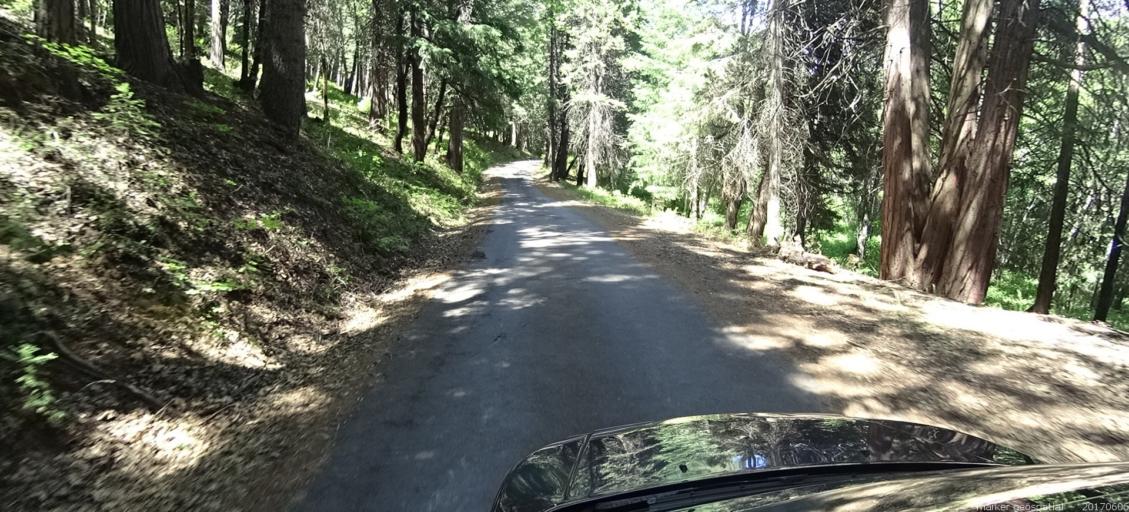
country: US
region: California
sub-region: Siskiyou County
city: Mount Shasta
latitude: 41.2691
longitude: -122.3061
